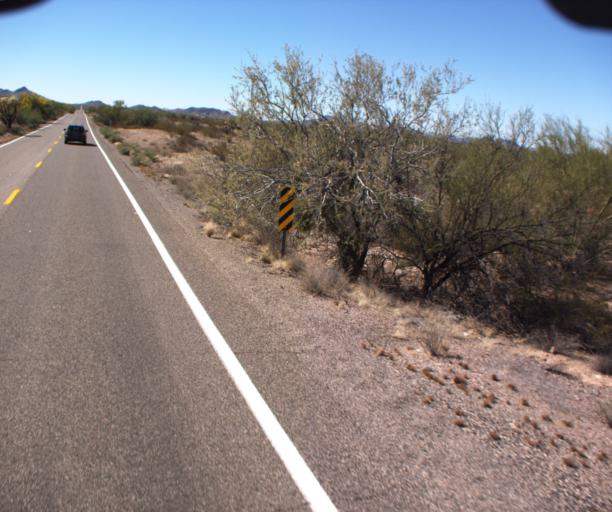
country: US
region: Arizona
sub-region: Pima County
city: Ajo
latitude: 32.1548
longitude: -112.7648
